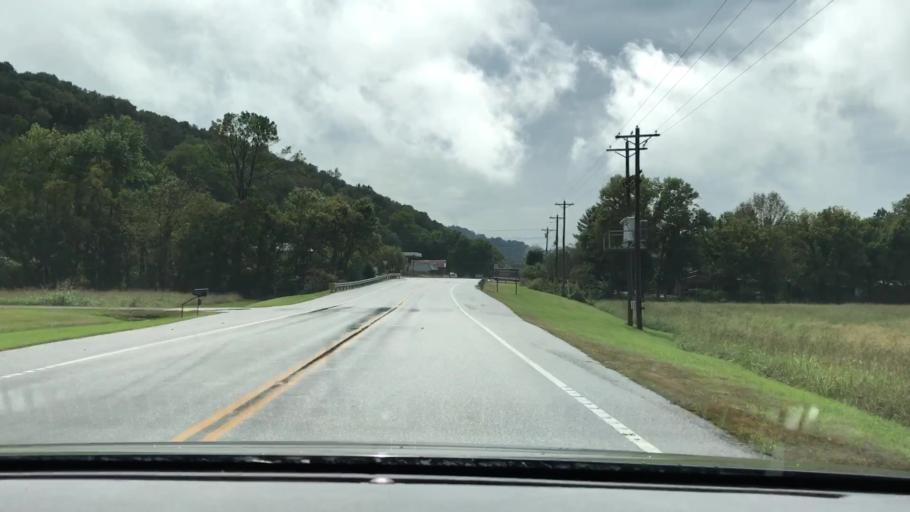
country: US
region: Tennessee
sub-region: Smith County
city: Carthage
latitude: 36.3199
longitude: -85.9686
